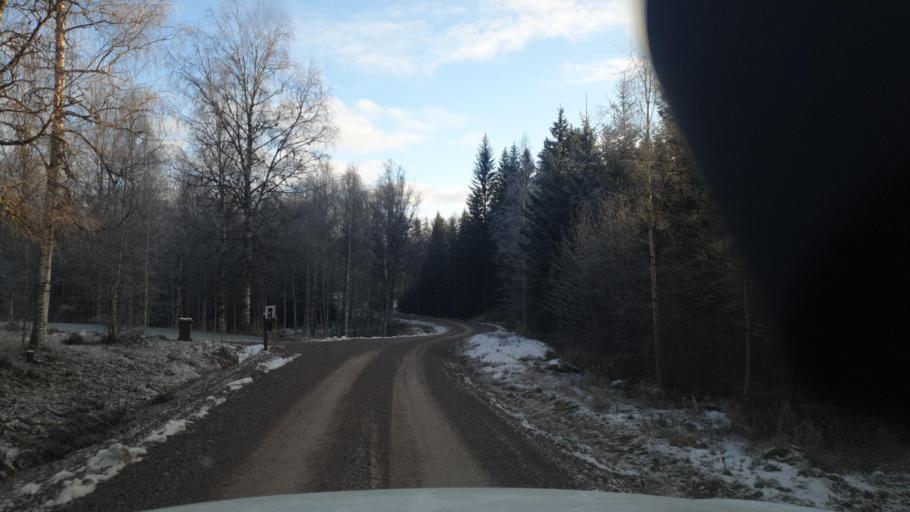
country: SE
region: Vaermland
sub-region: Eda Kommun
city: Charlottenberg
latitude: 60.0912
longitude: 12.5001
